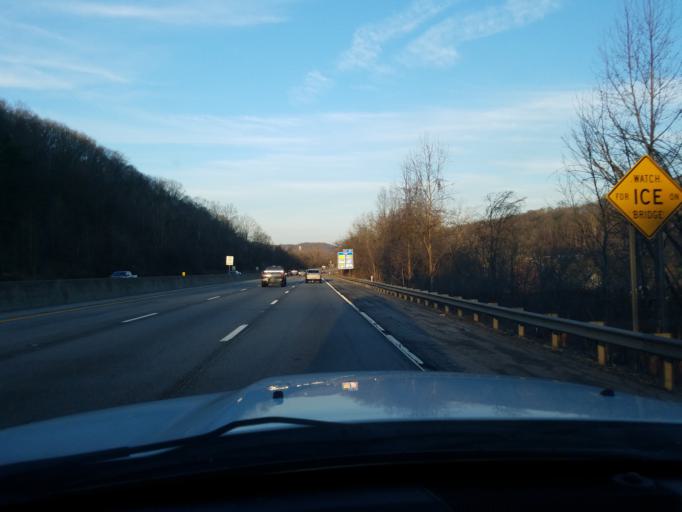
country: US
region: West Virginia
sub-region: Kanawha County
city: Nitro
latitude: 38.4275
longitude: -81.8191
